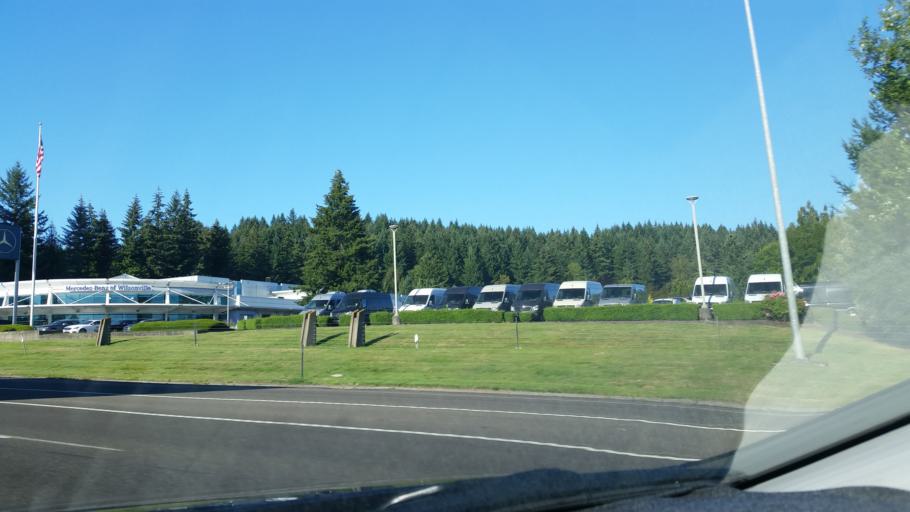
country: US
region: Oregon
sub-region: Clackamas County
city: Wilsonville
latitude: 45.3390
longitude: -122.7690
